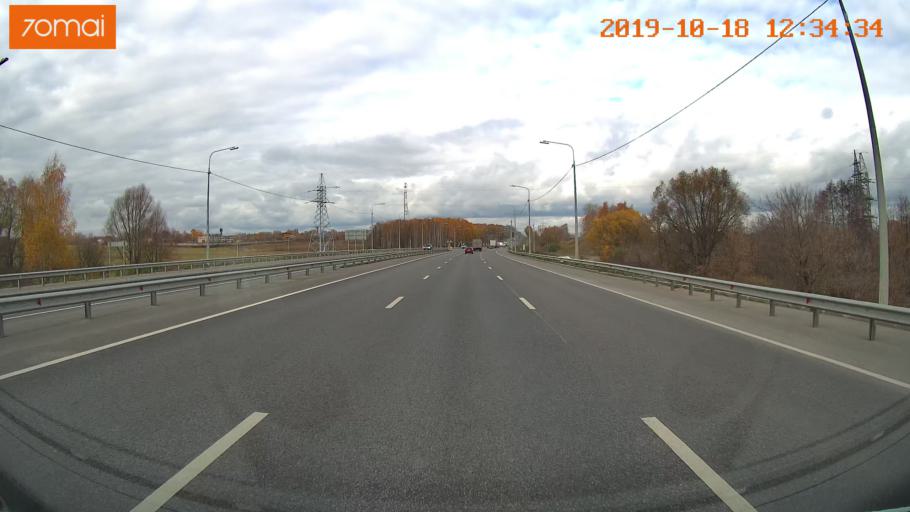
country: RU
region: Rjazan
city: Ryazan'
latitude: 54.6154
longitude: 39.6377
